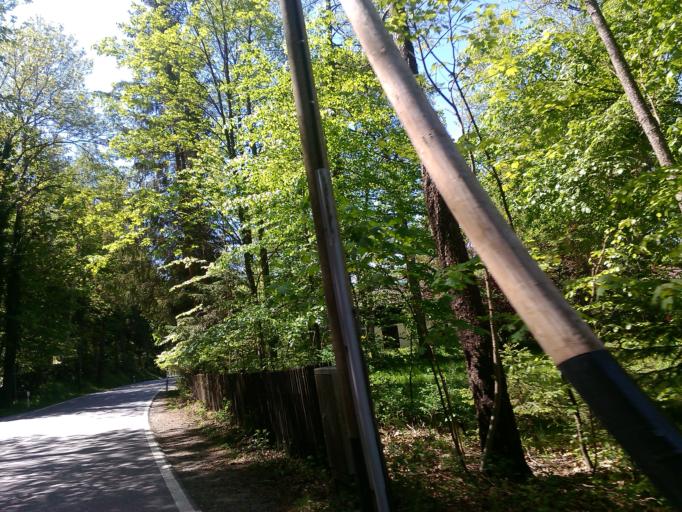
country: DE
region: Bavaria
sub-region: Upper Bavaria
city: Pocking
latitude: 47.9726
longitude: 11.3256
